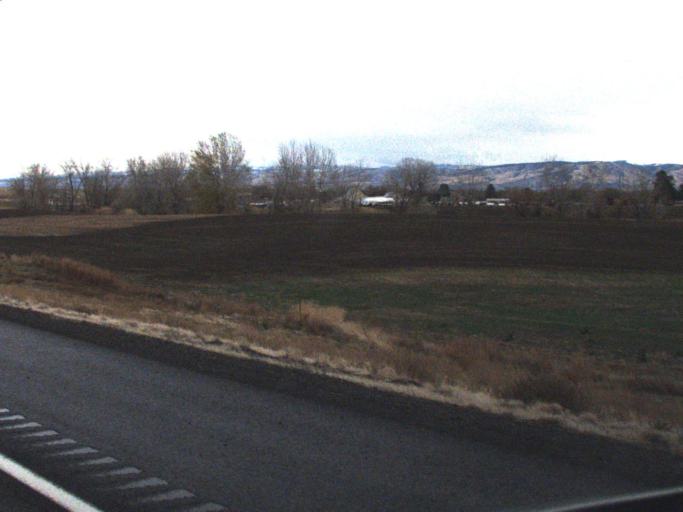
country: US
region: Washington
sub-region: Walla Walla County
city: Garrett
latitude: 46.0520
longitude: -118.4725
